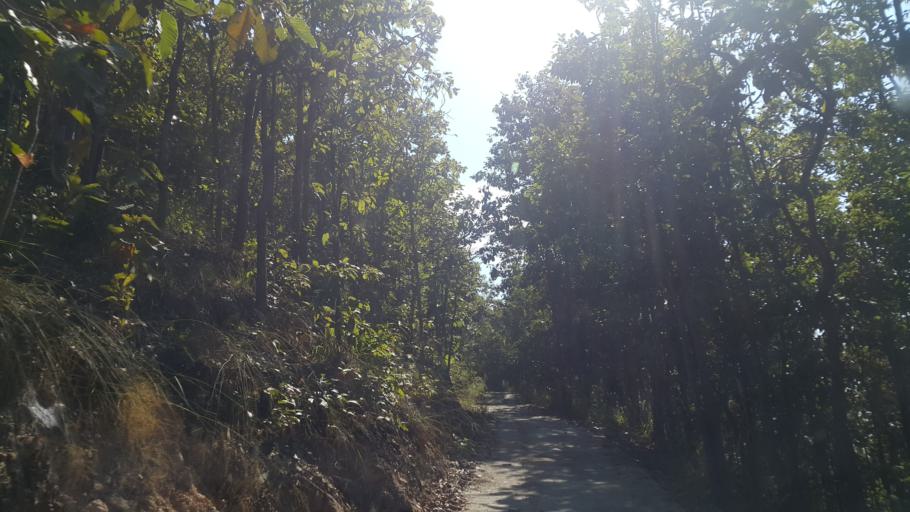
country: TH
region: Lamphun
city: Ban Thi
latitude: 18.6666
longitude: 99.1831
